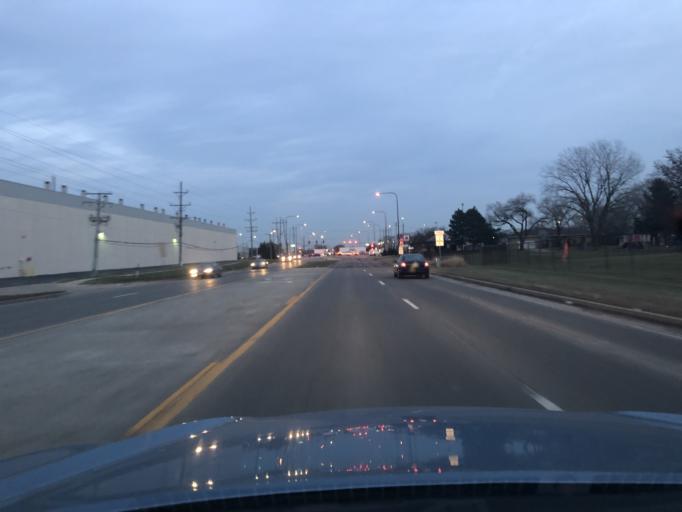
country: US
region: Illinois
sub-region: Cook County
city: Elk Grove Village
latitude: 41.9930
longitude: -87.9631
